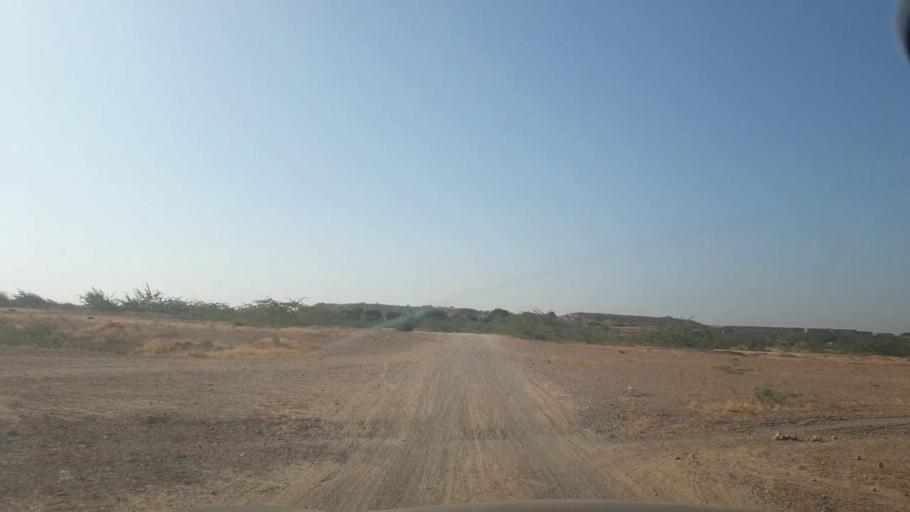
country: PK
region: Sindh
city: Malir Cantonment
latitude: 25.0373
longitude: 67.2607
